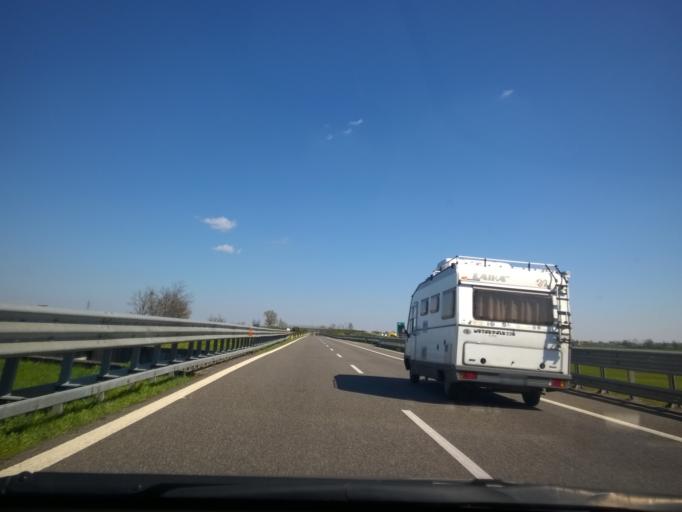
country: IT
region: Emilia-Romagna
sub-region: Provincia di Piacenza
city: Pontenure
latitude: 45.0500
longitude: 9.7748
